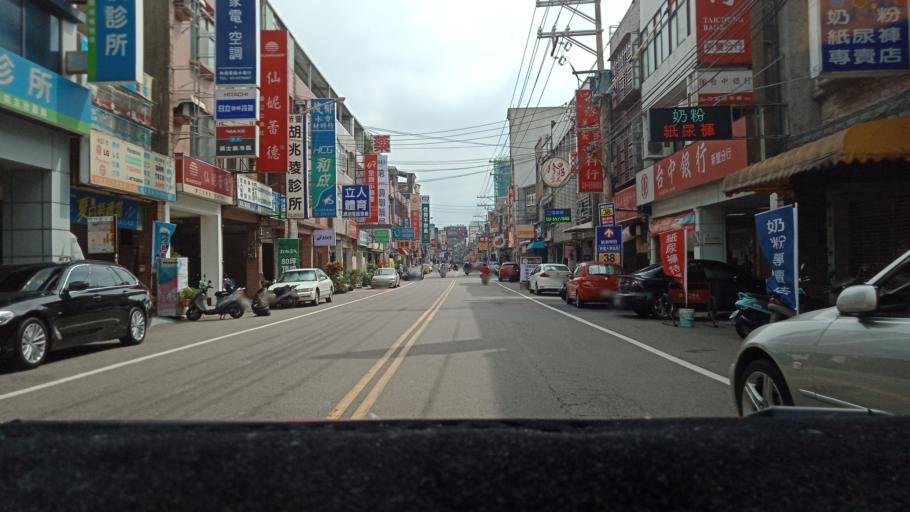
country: TW
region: Taiwan
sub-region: Hsinchu
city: Zhubei
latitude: 24.8749
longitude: 120.9945
